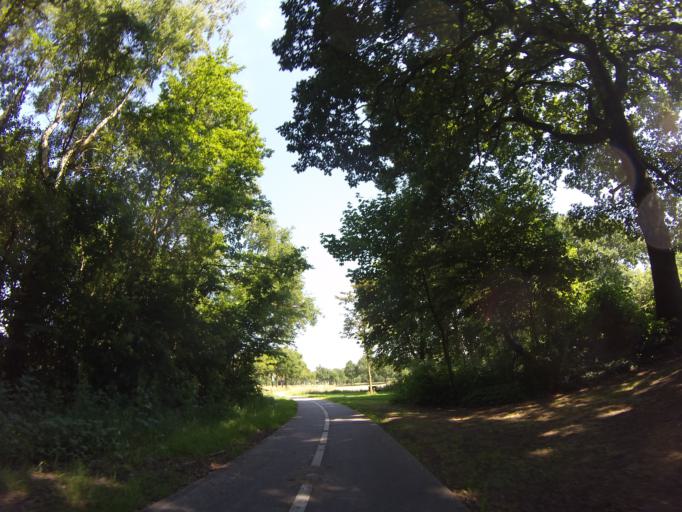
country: NL
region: Drenthe
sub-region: Gemeente Coevorden
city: Sleen
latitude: 52.7993
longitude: 6.7302
